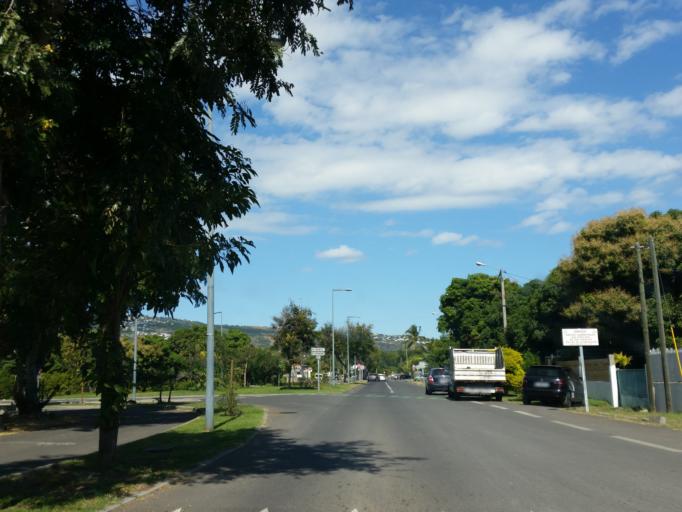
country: RE
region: Reunion
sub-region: Reunion
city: Saint-Paul
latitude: -20.9837
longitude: 55.2895
